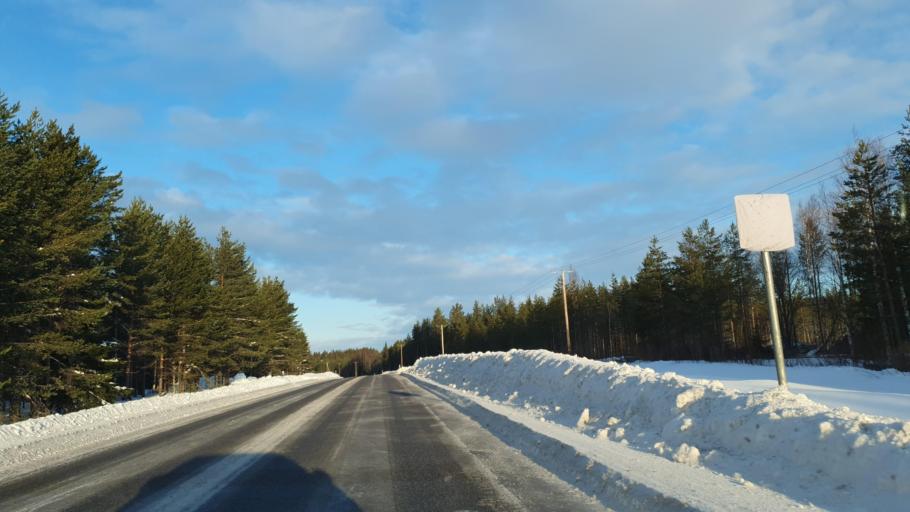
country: FI
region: Kainuu
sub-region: Kajaani
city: Vaala
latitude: 64.5435
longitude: 27.1822
